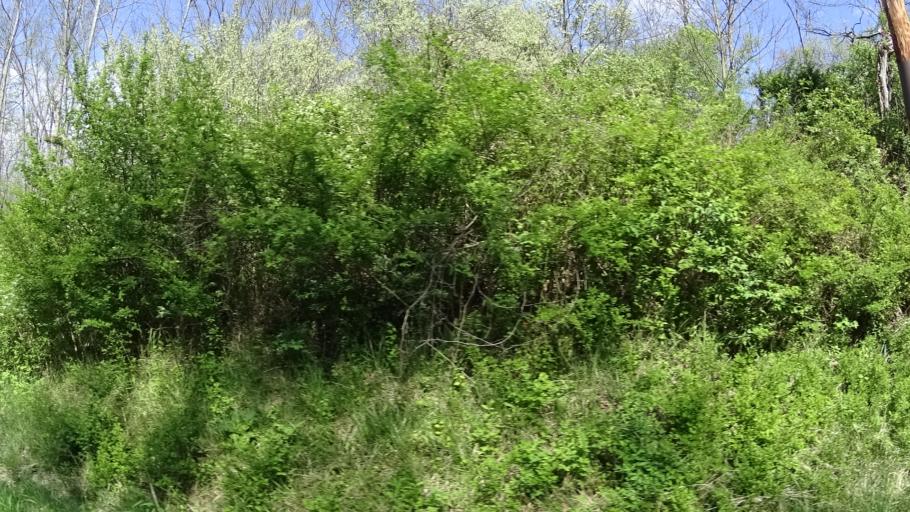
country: US
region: Ohio
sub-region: Lorain County
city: Lagrange
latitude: 41.2933
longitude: -82.1385
